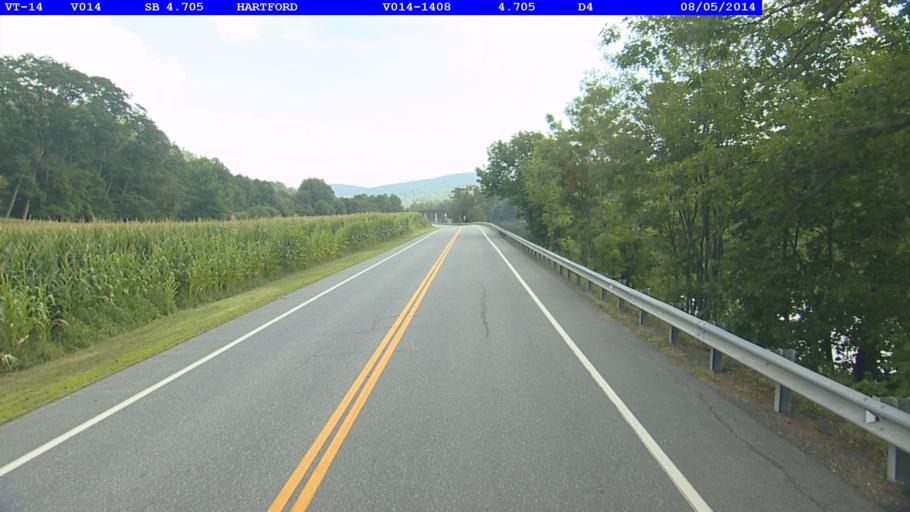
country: US
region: Vermont
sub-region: Windsor County
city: White River Junction
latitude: 43.6852
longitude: -72.3981
